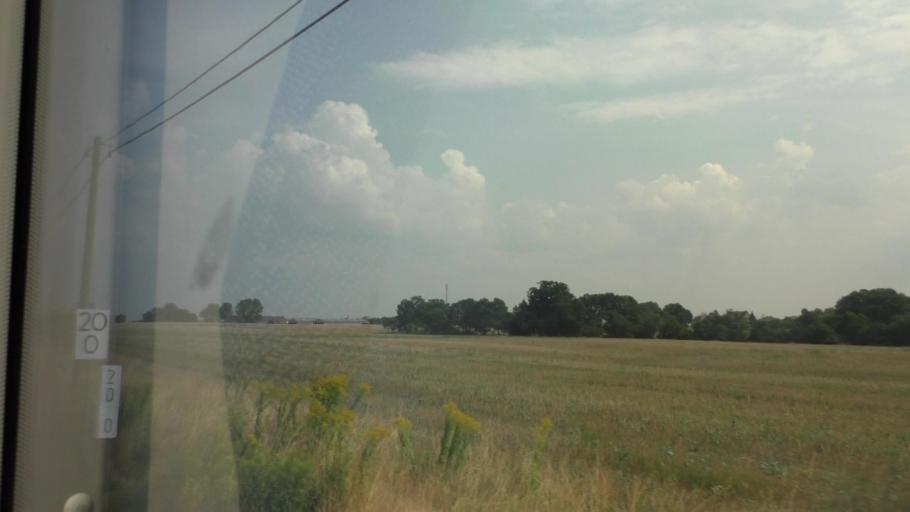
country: DE
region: Brandenburg
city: Rietz Neuendorf
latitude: 52.2039
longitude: 14.1178
